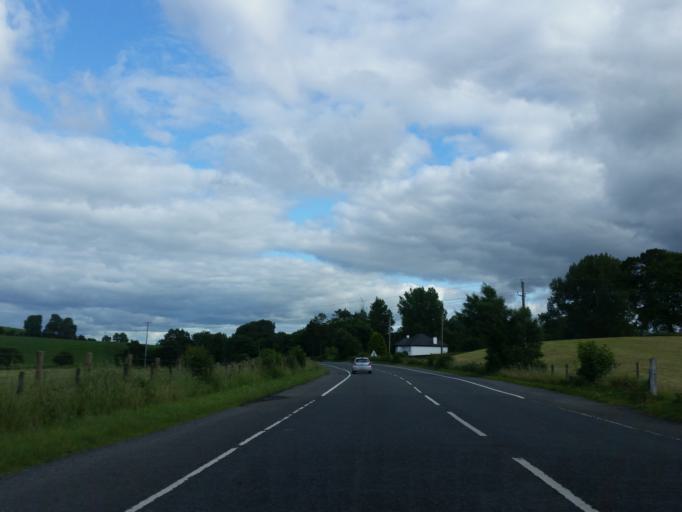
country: GB
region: Northern Ireland
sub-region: Fermanagh District
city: Enniskillen
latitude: 54.3227
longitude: -7.5978
